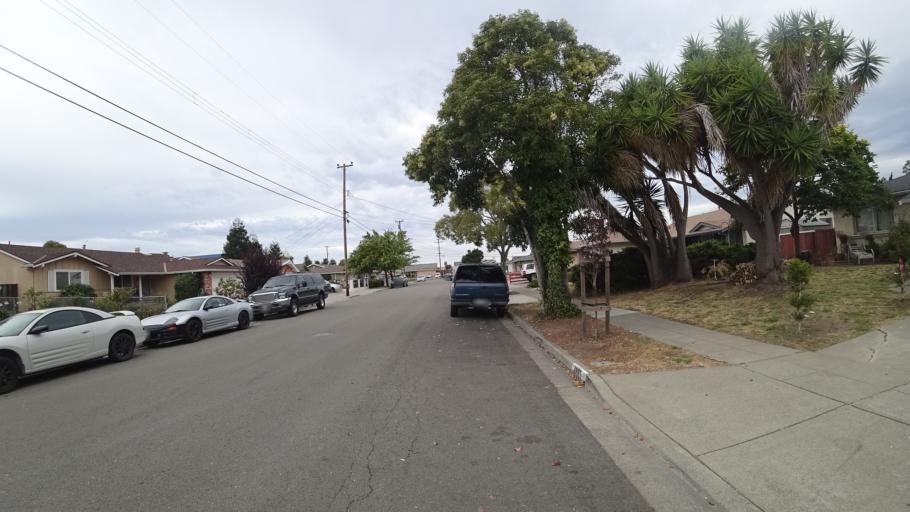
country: US
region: California
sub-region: Alameda County
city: Hayward
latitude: 37.6196
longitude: -122.0835
